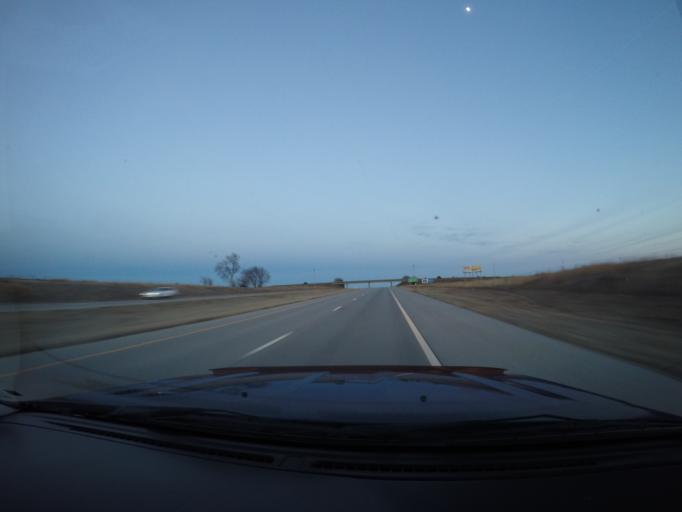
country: US
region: Kansas
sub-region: Geary County
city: Junction City
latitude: 39.0006
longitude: -96.9038
